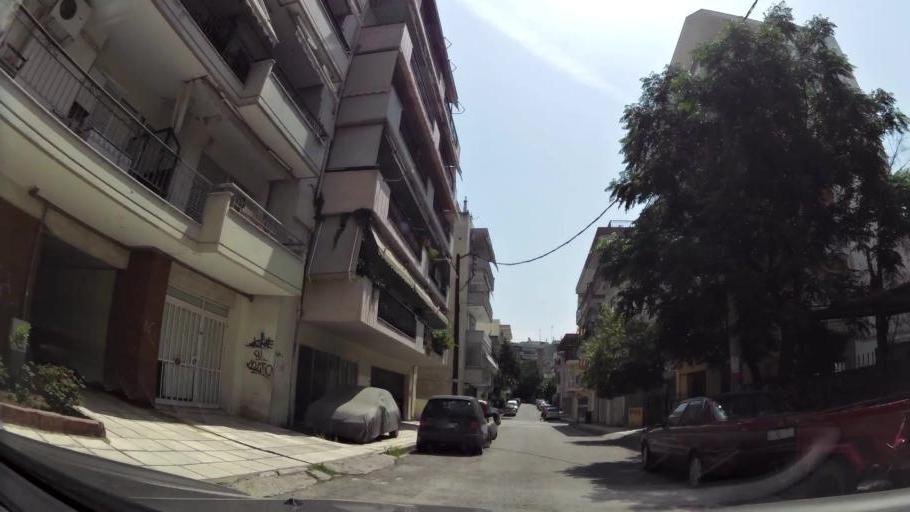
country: GR
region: Central Macedonia
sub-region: Nomos Thessalonikis
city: Evosmos
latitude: 40.6726
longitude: 22.9064
